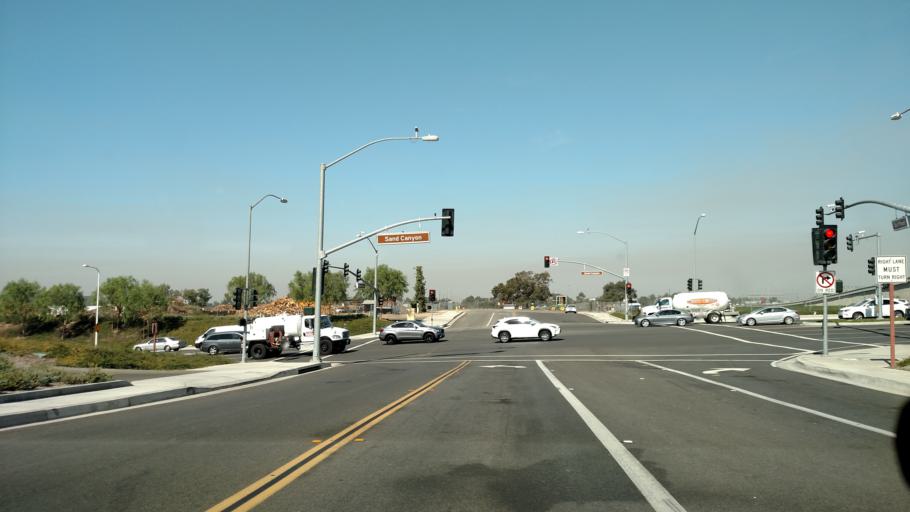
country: US
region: California
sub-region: Orange County
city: Irvine
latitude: 33.6766
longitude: -117.7588
